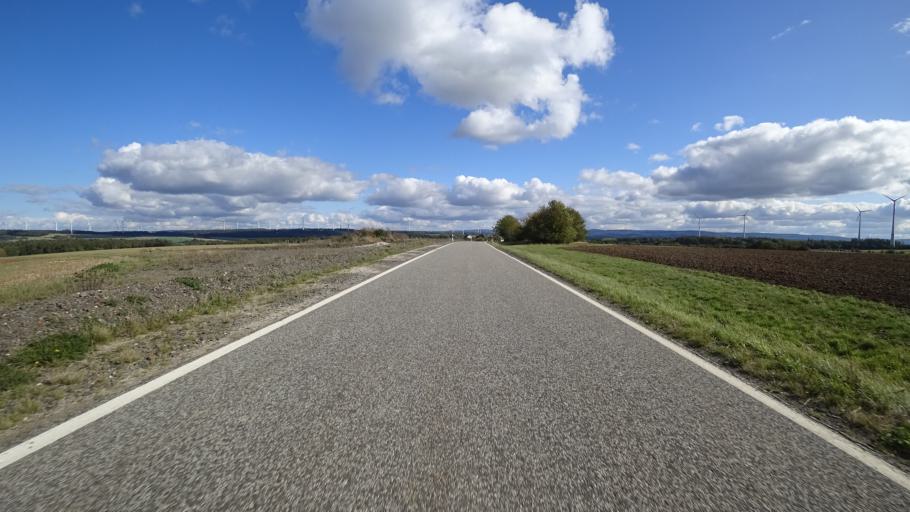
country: DE
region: Rheinland-Pfalz
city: Michelbach
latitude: 50.0160
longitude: 7.4428
